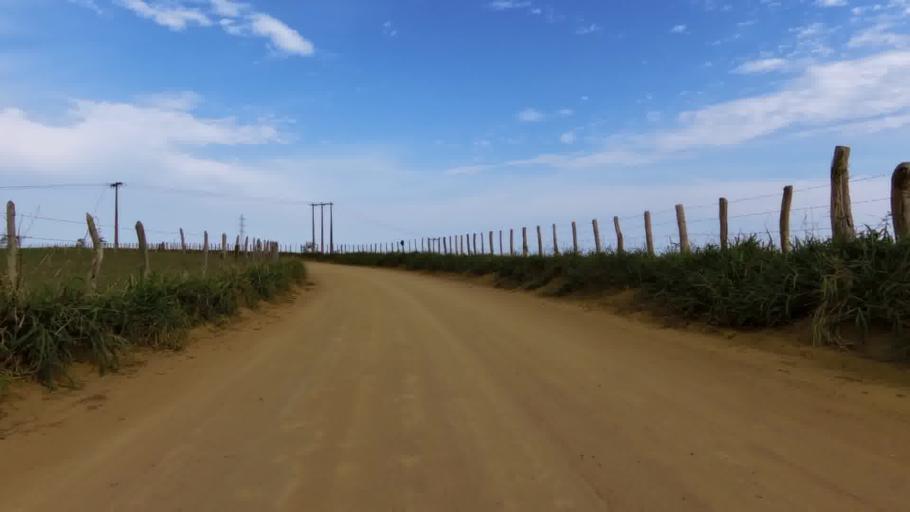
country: BR
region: Espirito Santo
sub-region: Piuma
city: Piuma
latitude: -20.8262
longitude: -40.7463
